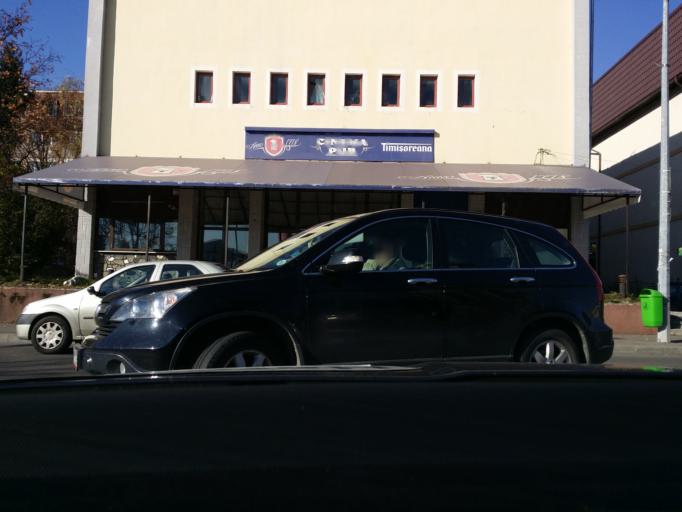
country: RO
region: Prahova
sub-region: Municipiul Campina
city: Campina
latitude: 45.1285
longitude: 25.7334
